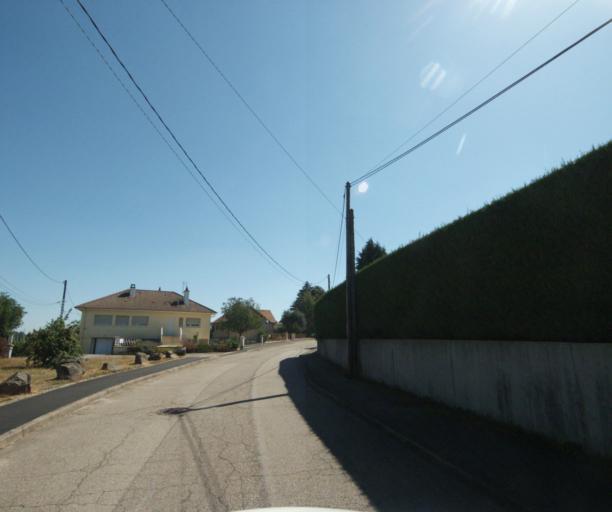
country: FR
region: Lorraine
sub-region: Departement des Vosges
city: Epinal
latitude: 48.1797
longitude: 6.4696
